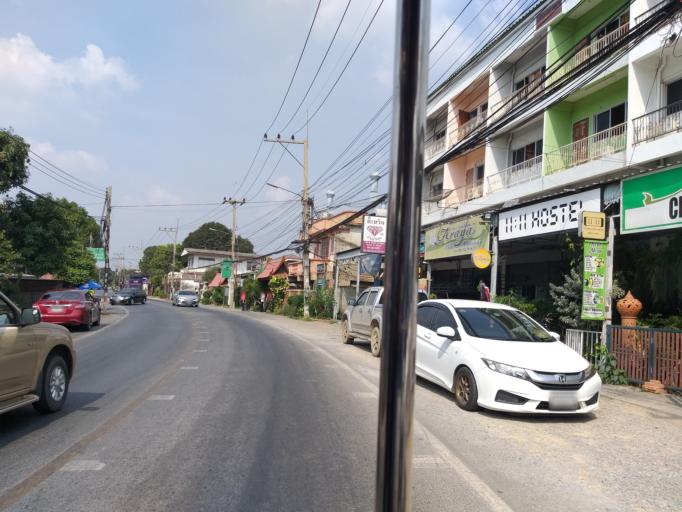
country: TH
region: Phra Nakhon Si Ayutthaya
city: Phra Nakhon Si Ayutthaya
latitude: 14.3484
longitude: 100.5811
